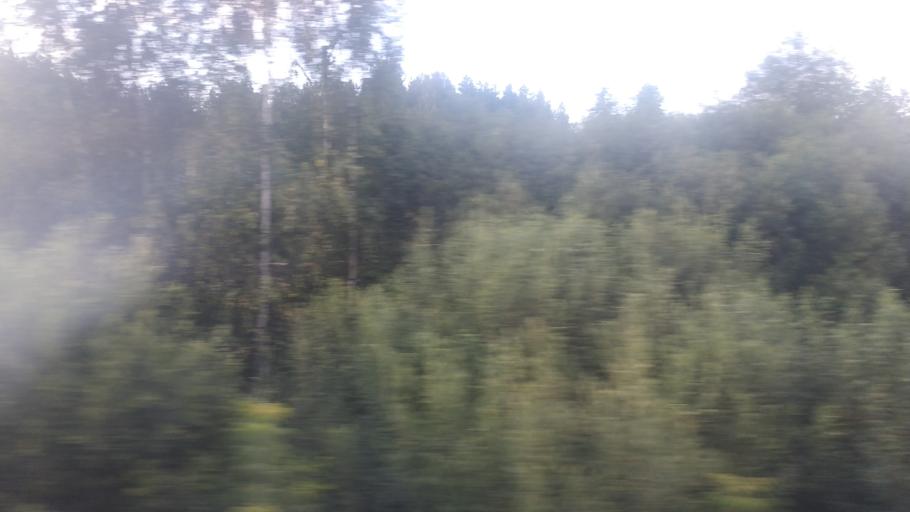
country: RU
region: Moskovskaya
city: Tugolesskiy Bor
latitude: 55.5596
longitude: 39.6997
